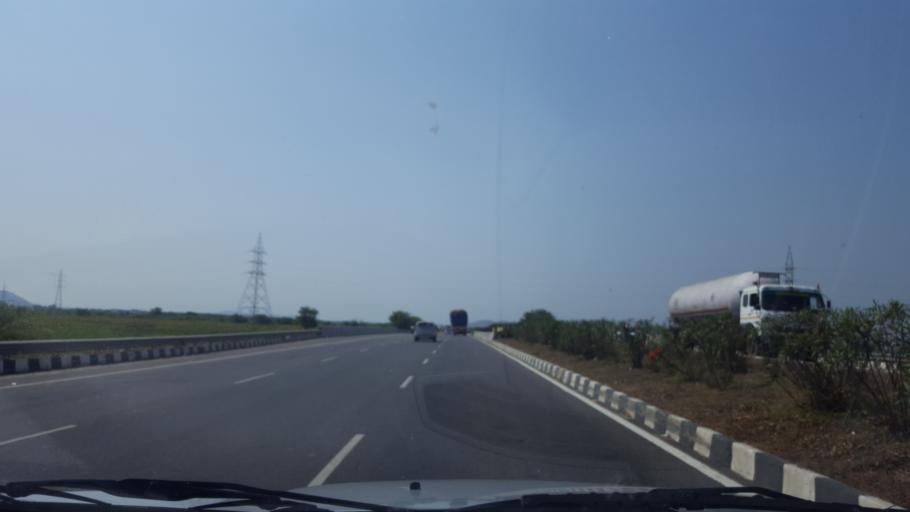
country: IN
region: Andhra Pradesh
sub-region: Guntur
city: Chilakalurupet
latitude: 16.0252
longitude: 80.1263
